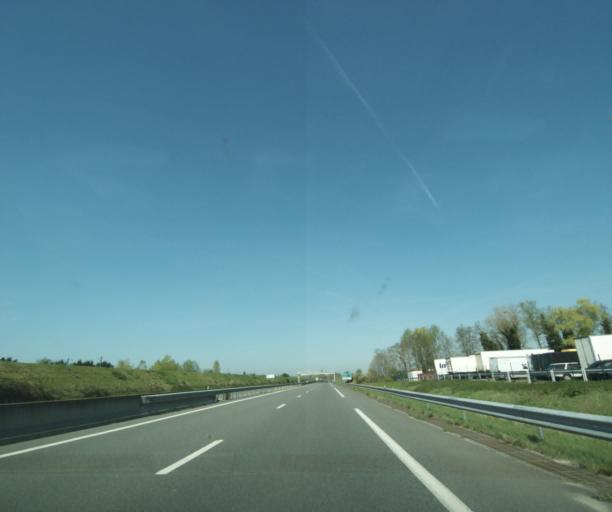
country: FR
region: Auvergne
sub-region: Departement de l'Allier
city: Avermes
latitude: 46.6017
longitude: 3.3030
